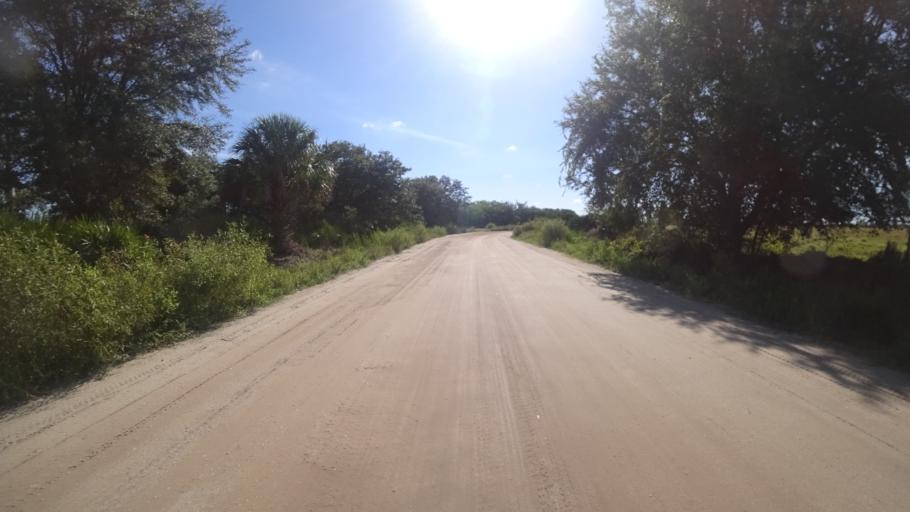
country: US
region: Florida
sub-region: Sarasota County
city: The Meadows
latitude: 27.4726
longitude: -82.3455
